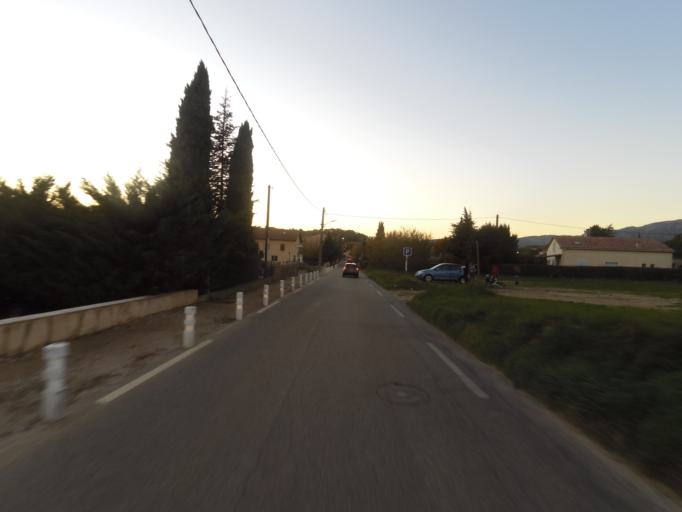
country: FR
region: Provence-Alpes-Cote d'Azur
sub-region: Departement du Vaucluse
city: Bedoin
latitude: 44.1247
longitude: 5.1835
